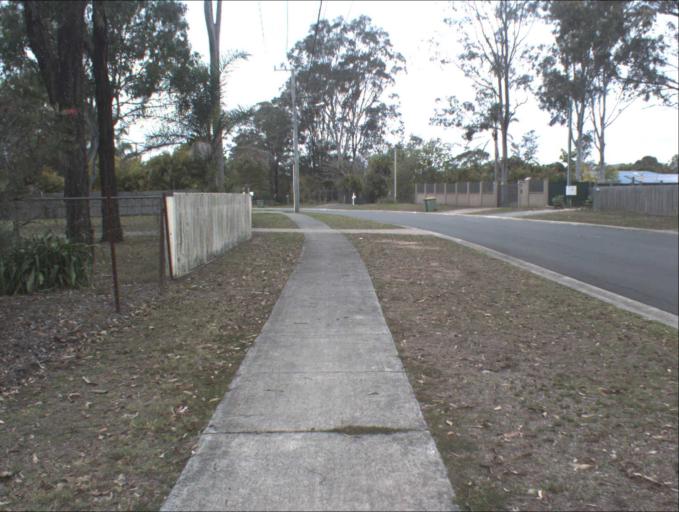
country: AU
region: Queensland
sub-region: Logan
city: Waterford West
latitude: -27.7028
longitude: 153.1390
